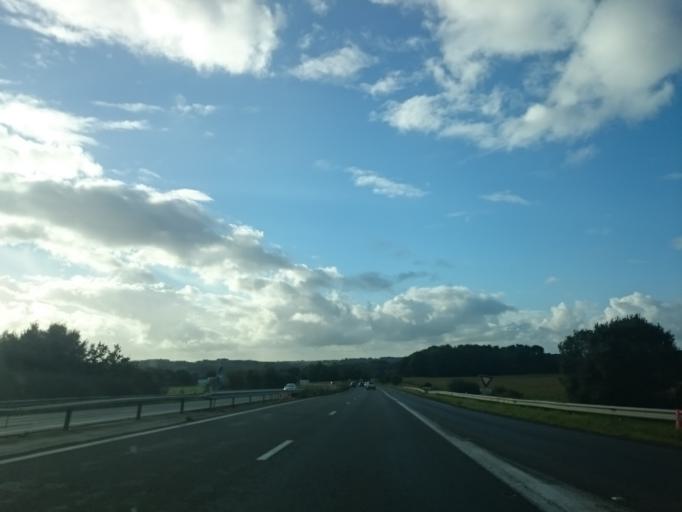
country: FR
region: Brittany
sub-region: Departement du Finistere
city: Morlaix
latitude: 48.5946
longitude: -3.8234
